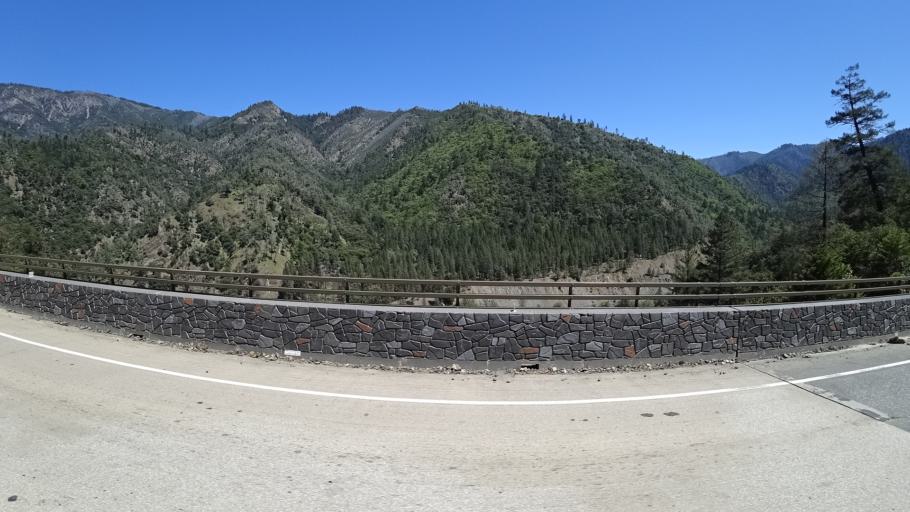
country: US
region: California
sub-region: Humboldt County
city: Willow Creek
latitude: 40.7989
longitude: -123.4633
